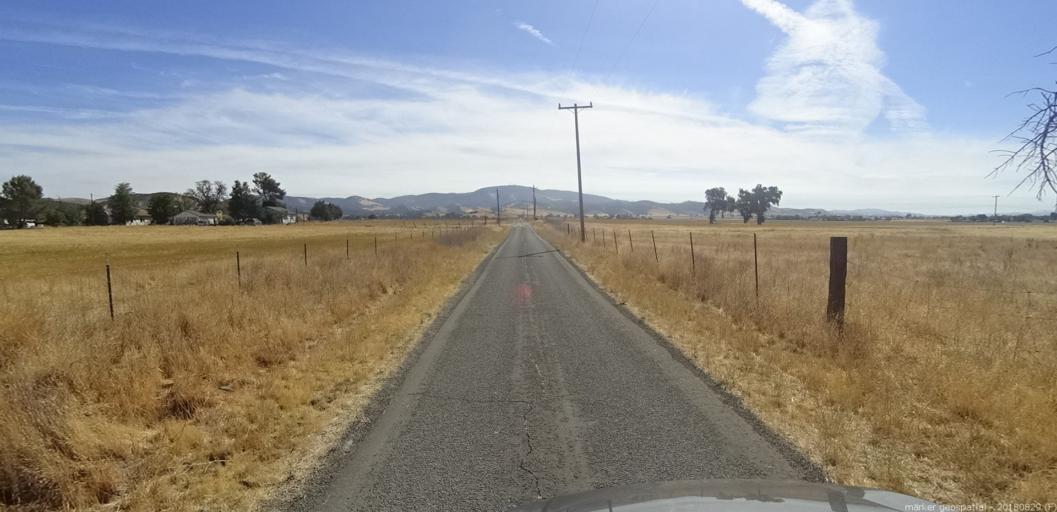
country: US
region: California
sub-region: Monterey County
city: King City
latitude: 35.9514
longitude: -121.0911
